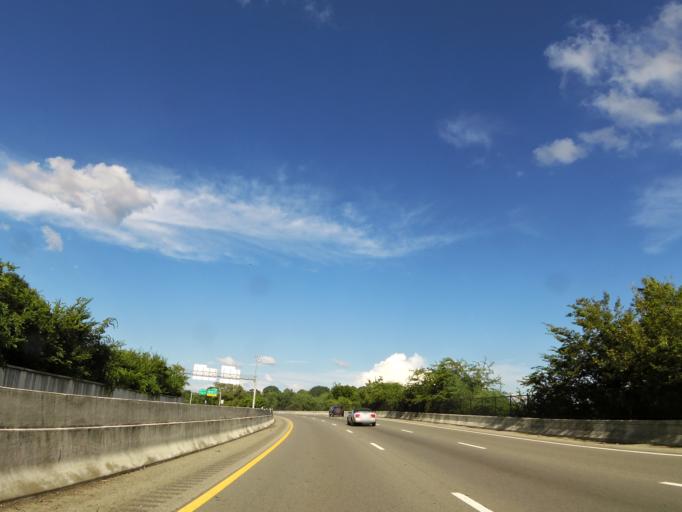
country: US
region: Tennessee
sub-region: Davidson County
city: Nashville
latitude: 36.2397
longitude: -86.7724
